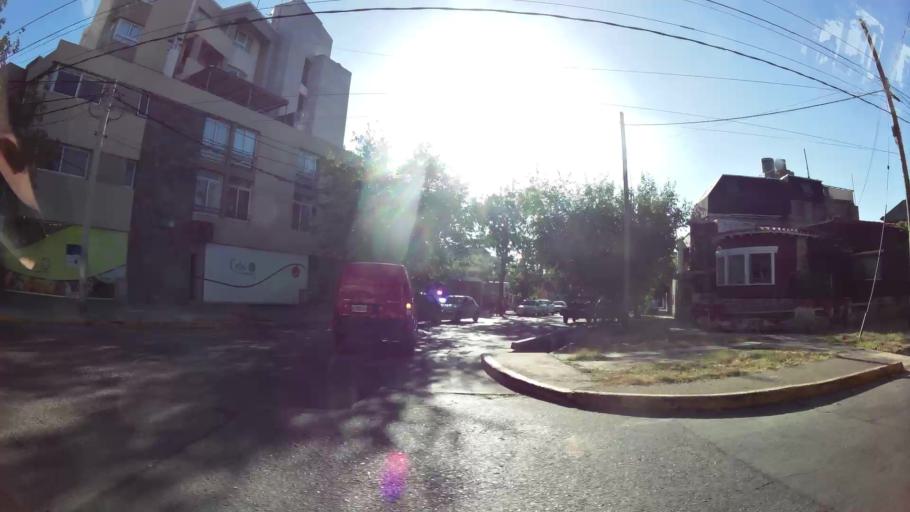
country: AR
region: Mendoza
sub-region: Departamento de Godoy Cruz
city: Godoy Cruz
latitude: -32.9091
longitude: -68.8512
